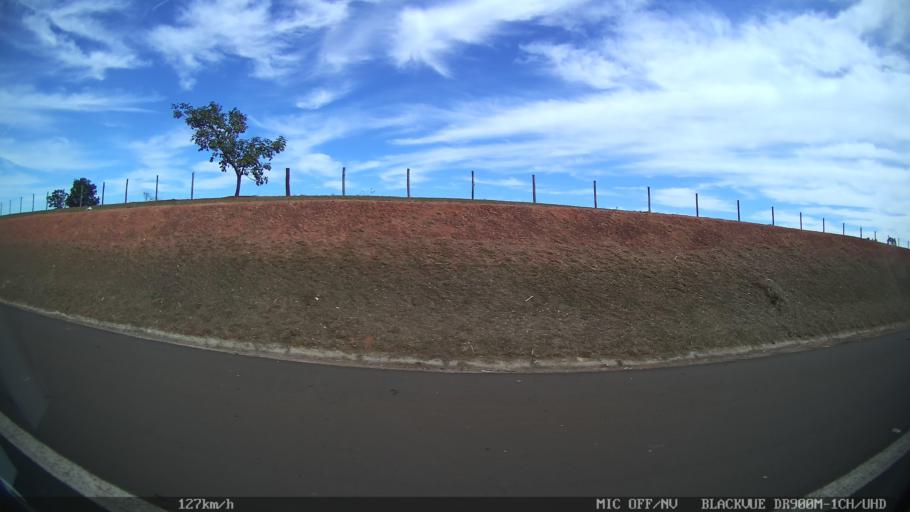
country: BR
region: Sao Paulo
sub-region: Matao
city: Matao
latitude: -21.5830
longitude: -48.4501
